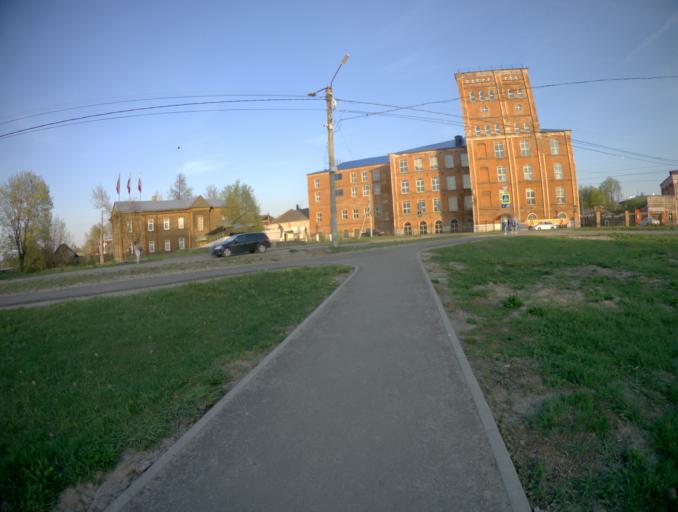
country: RU
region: Ivanovo
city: Yuzha
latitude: 56.5842
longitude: 42.0160
